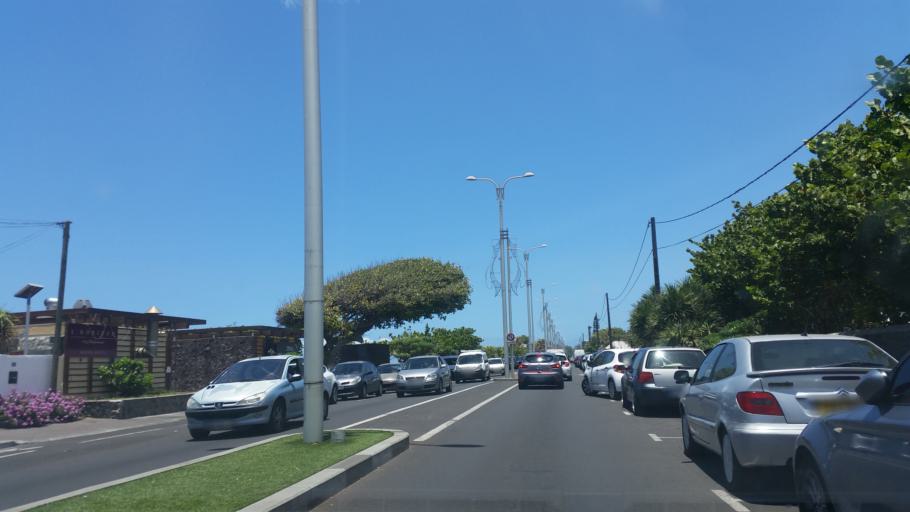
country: RE
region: Reunion
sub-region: Reunion
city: Saint-Pierre
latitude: -21.3434
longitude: 55.4678
